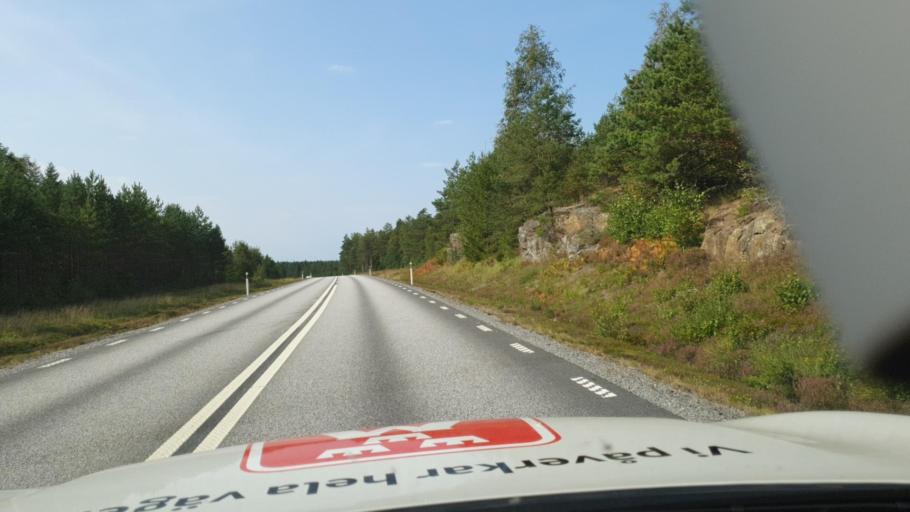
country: SE
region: Vaestra Goetaland
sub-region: Dals-Ed Kommun
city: Ed
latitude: 58.8395
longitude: 11.6264
